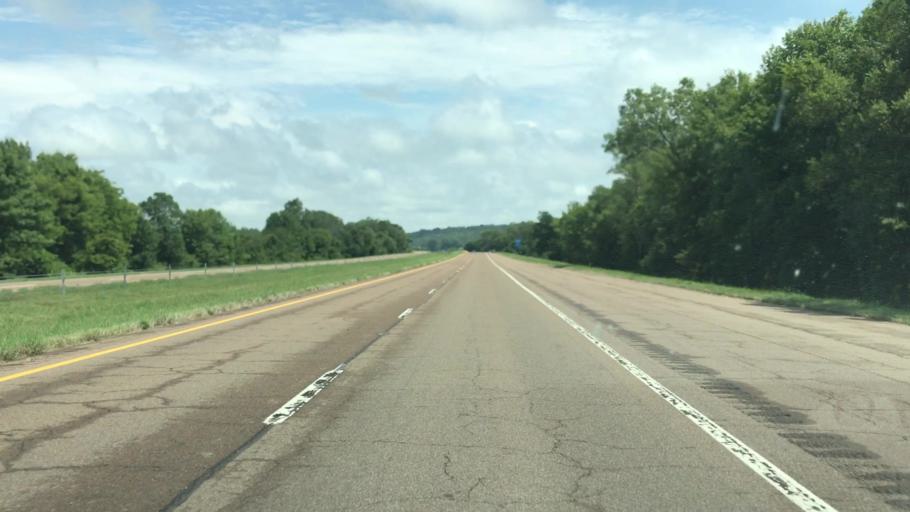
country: US
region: Tennessee
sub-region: Dyer County
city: Dyersburg
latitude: 36.0792
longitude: -89.5226
